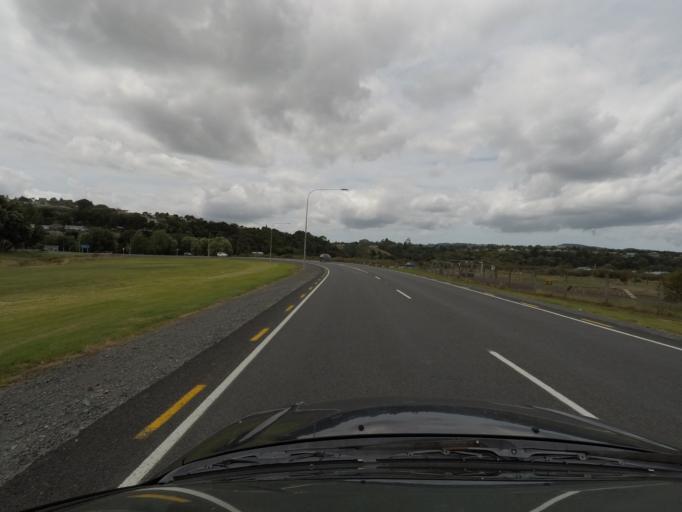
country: NZ
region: Northland
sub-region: Whangarei
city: Whangarei
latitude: -35.7341
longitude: 174.3422
